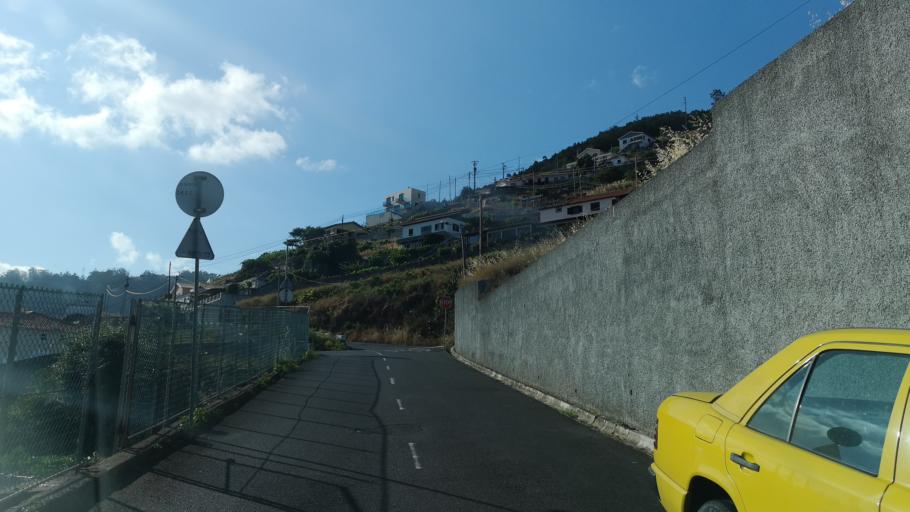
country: PT
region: Madeira
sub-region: Santa Cruz
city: Camacha
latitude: 32.6569
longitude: -16.8355
